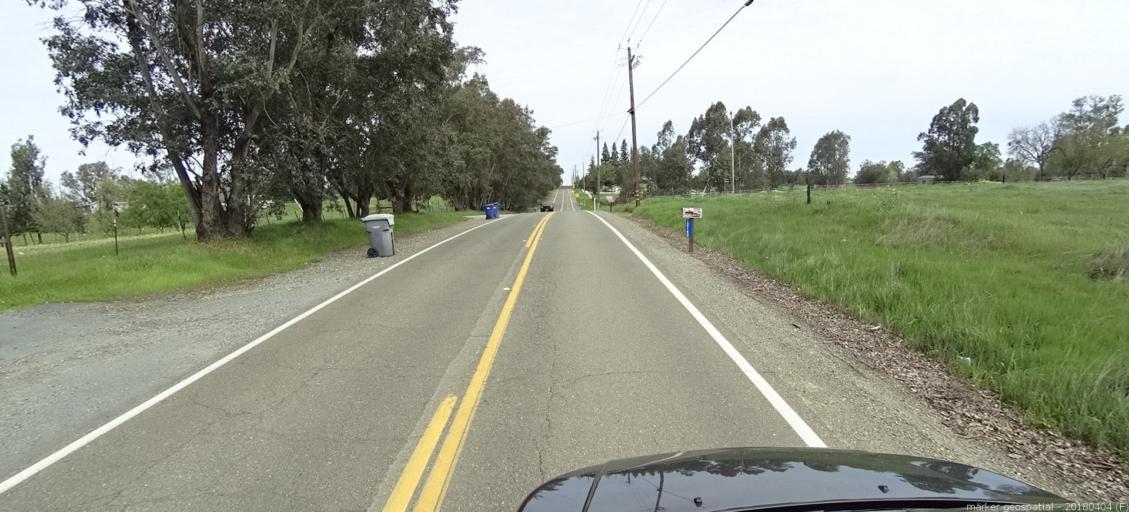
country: US
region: California
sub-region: Sacramento County
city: Clay
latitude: 38.3168
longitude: -121.1713
